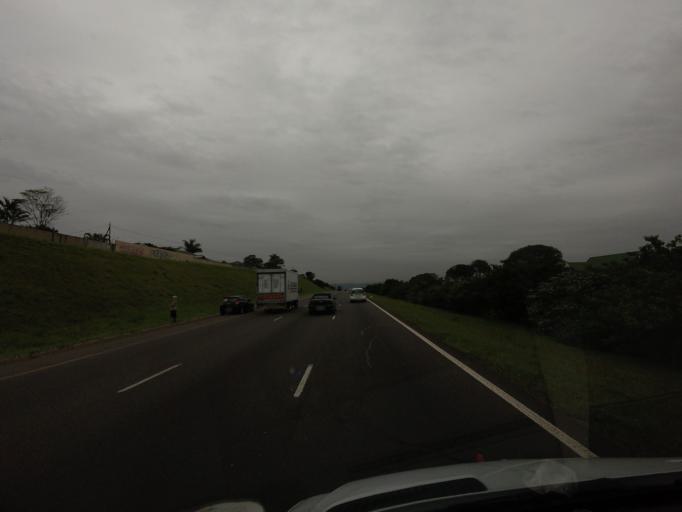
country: ZA
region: KwaZulu-Natal
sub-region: eThekwini Metropolitan Municipality
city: Durban
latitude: -29.7370
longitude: 31.0507
